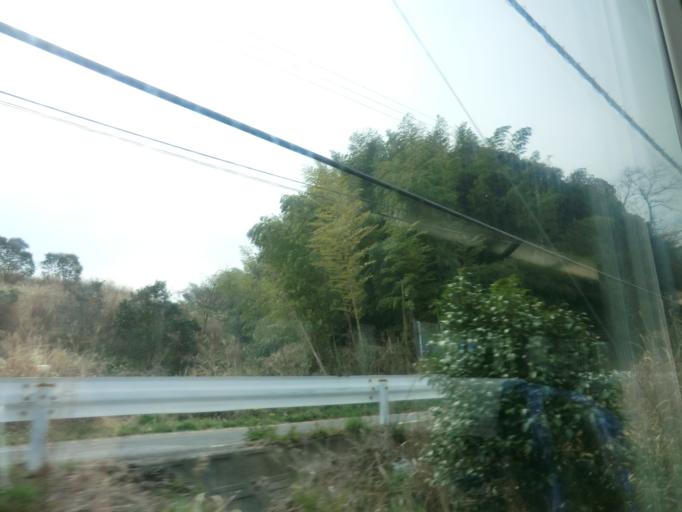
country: JP
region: Chiba
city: Ichihara
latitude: 35.4612
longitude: 140.0159
